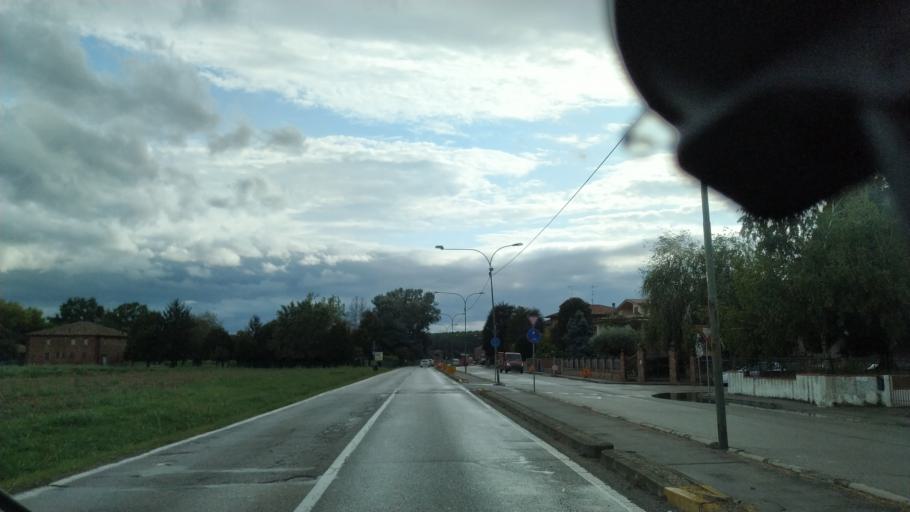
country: IT
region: Emilia-Romagna
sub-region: Provincia di Ferrara
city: Mirabello
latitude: 44.8212
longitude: 11.4549
